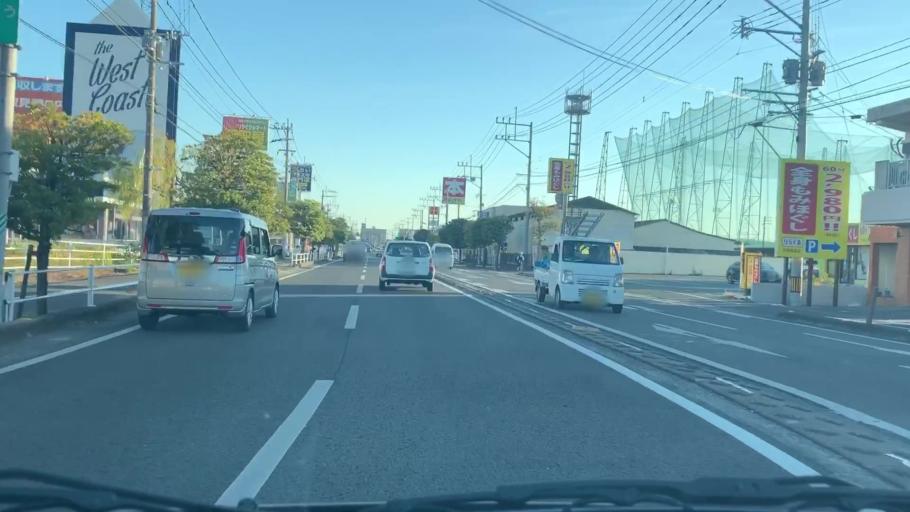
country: JP
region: Saga Prefecture
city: Saga-shi
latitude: 33.2666
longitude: 130.2718
